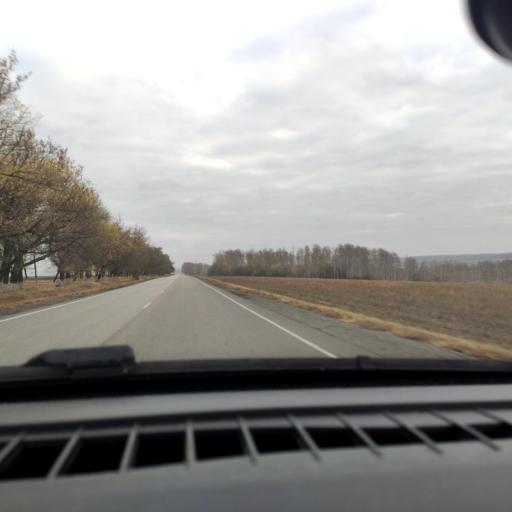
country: RU
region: Belgorod
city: Ilovka
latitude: 50.7576
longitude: 38.7295
